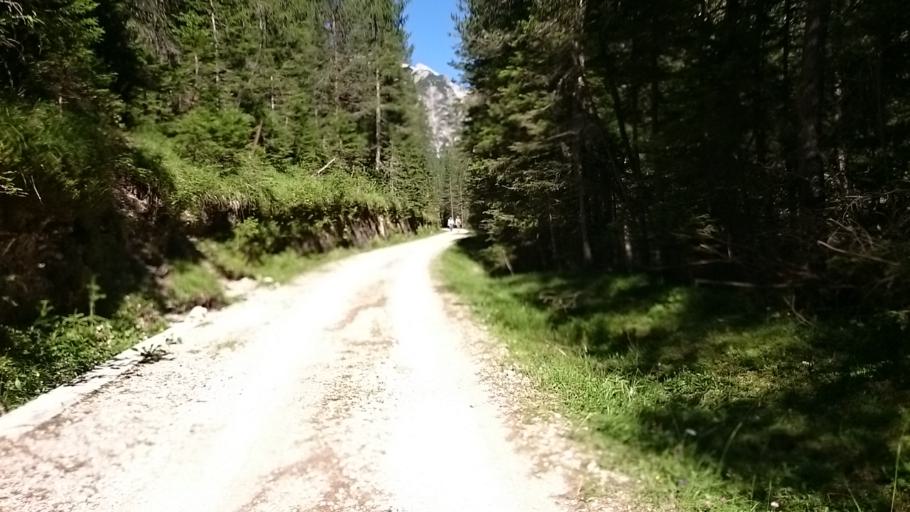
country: IT
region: Veneto
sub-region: Provincia di Belluno
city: Cortina d'Ampezzo
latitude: 46.6198
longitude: 12.1998
